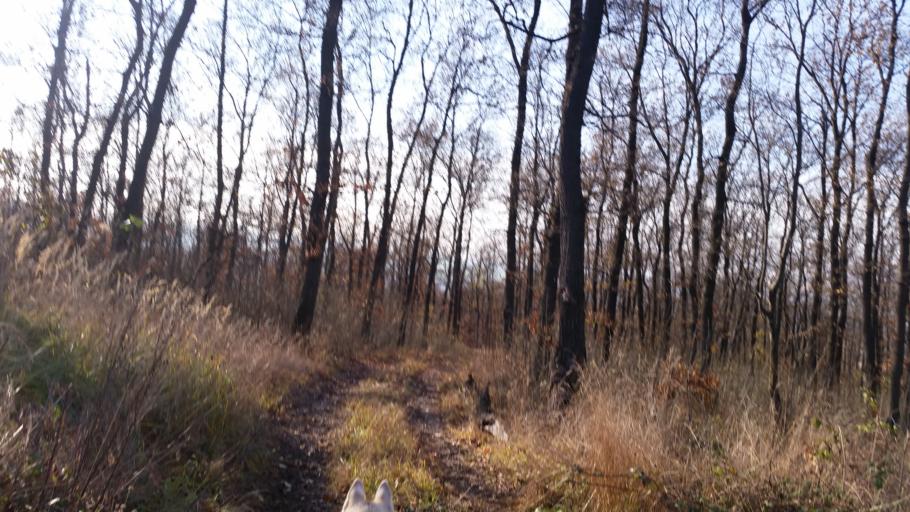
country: HU
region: Pest
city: Telki
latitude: 47.5678
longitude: 18.8242
